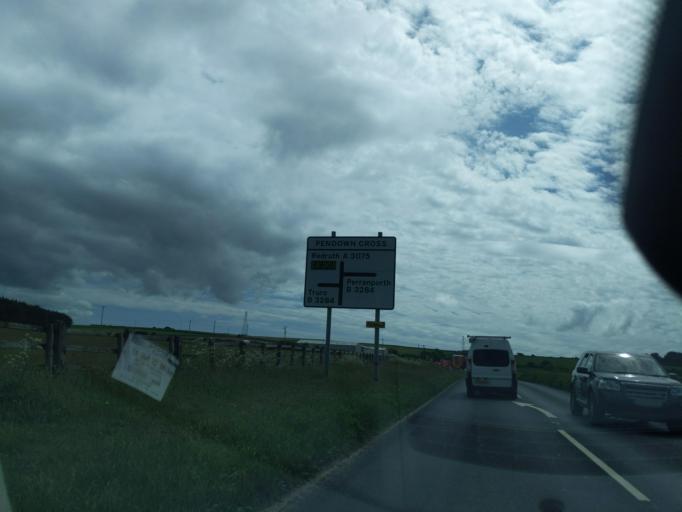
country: GB
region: England
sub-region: Cornwall
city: Perranporth
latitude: 50.3001
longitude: -5.1451
